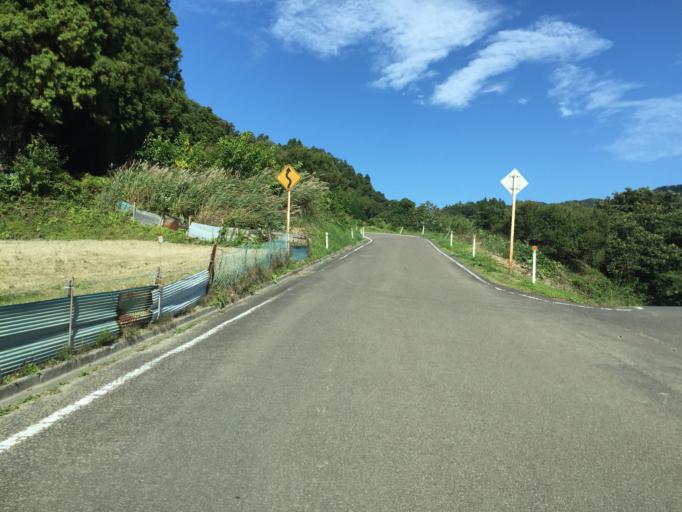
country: JP
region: Fukushima
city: Yanagawamachi-saiwaicho
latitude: 37.8524
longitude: 140.6719
